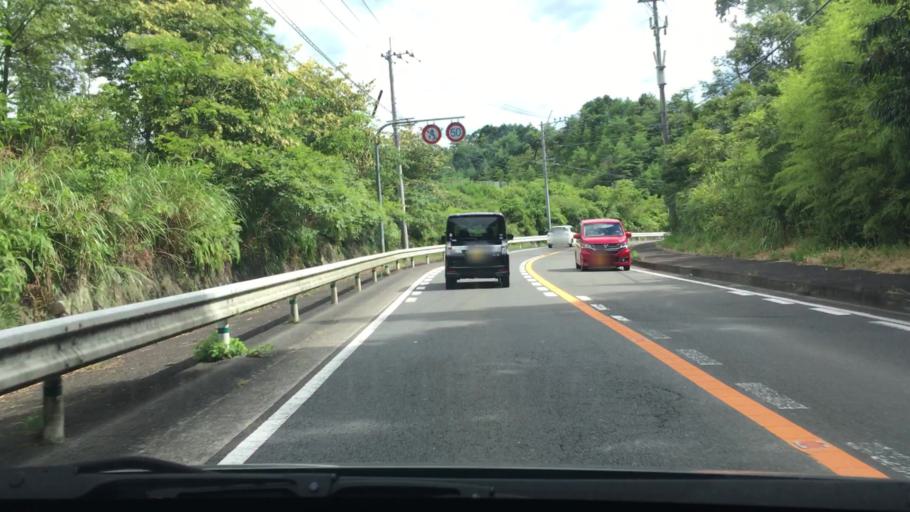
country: JP
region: Nagasaki
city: Togitsu
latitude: 32.9608
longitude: 129.7836
